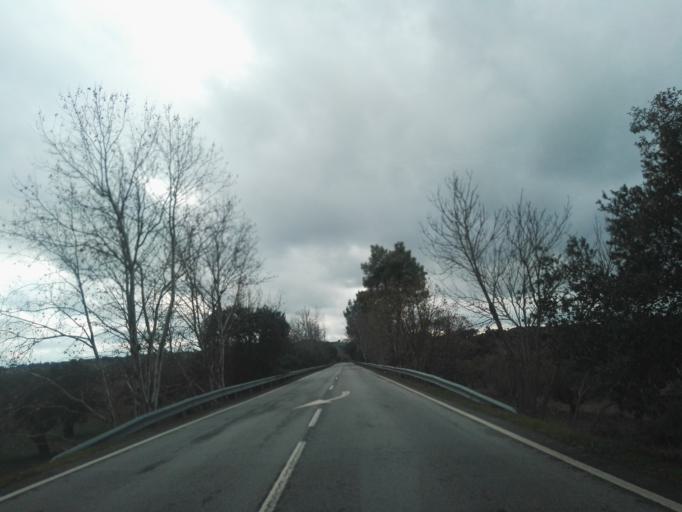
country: PT
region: Portalegre
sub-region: Arronches
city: Arronches
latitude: 39.0975
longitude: -7.2805
